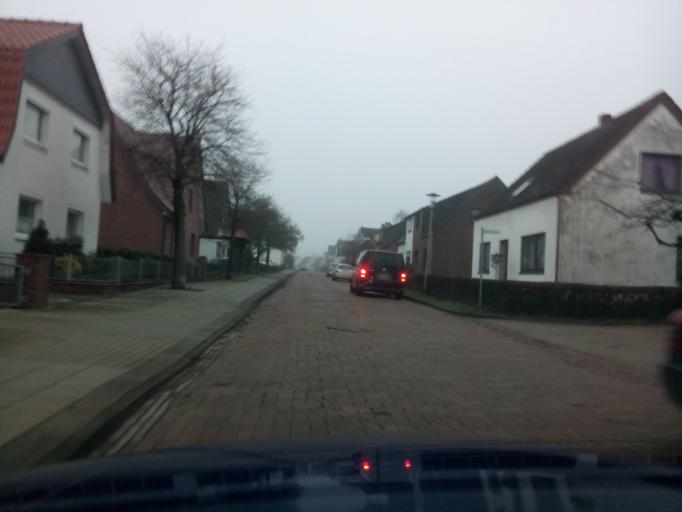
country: DE
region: Lower Saxony
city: Osterholz-Scharmbeck
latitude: 53.2191
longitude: 8.7884
